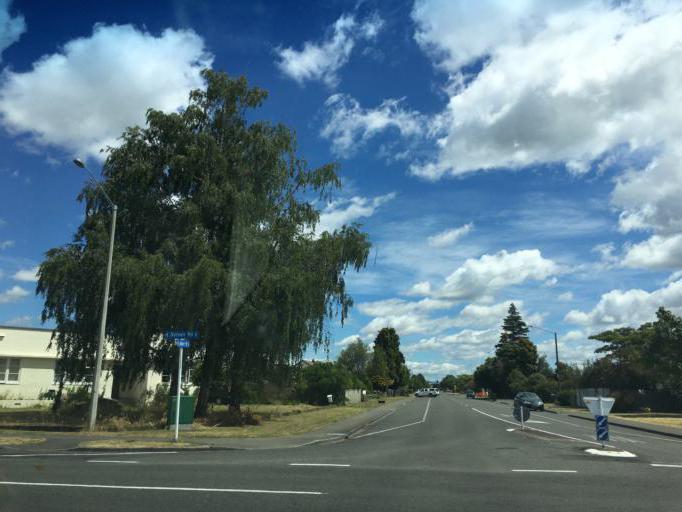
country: NZ
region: Hawke's Bay
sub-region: Hastings District
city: Hastings
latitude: -39.6455
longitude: 176.8578
